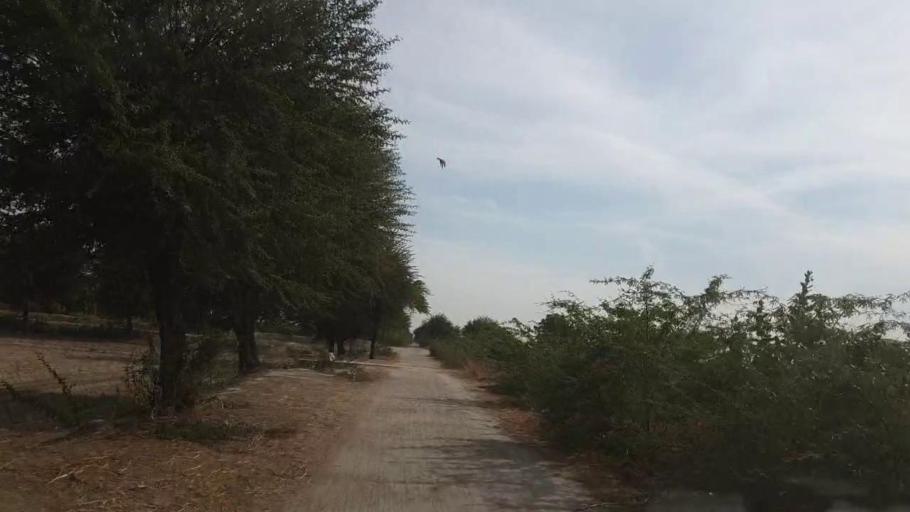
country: PK
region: Sindh
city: Nabisar
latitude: 25.0242
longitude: 69.5623
